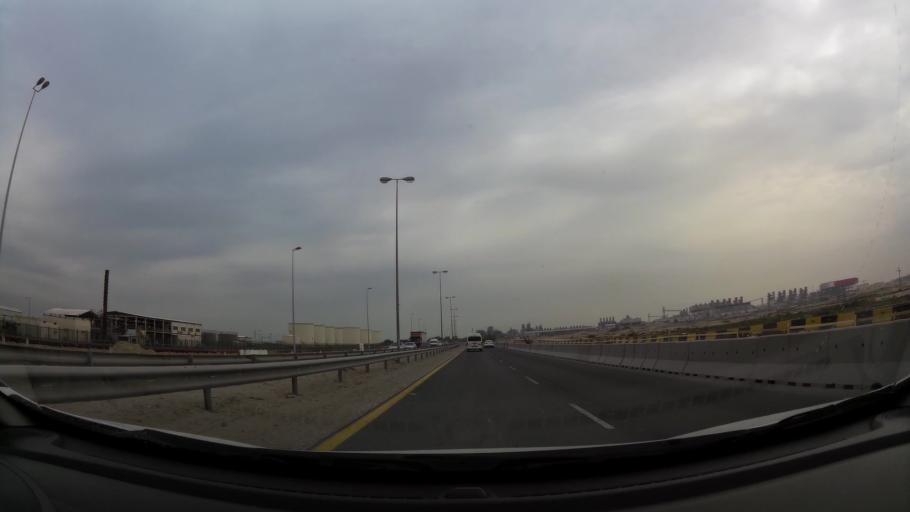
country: BH
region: Northern
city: Ar Rifa'
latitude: 26.1038
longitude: 50.6019
